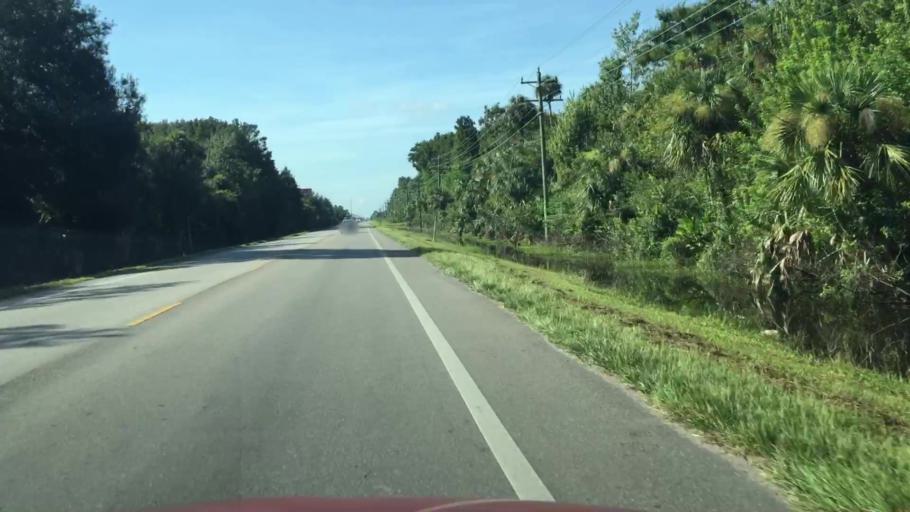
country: US
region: Florida
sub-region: Collier County
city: Immokalee
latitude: 26.4064
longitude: -81.4172
